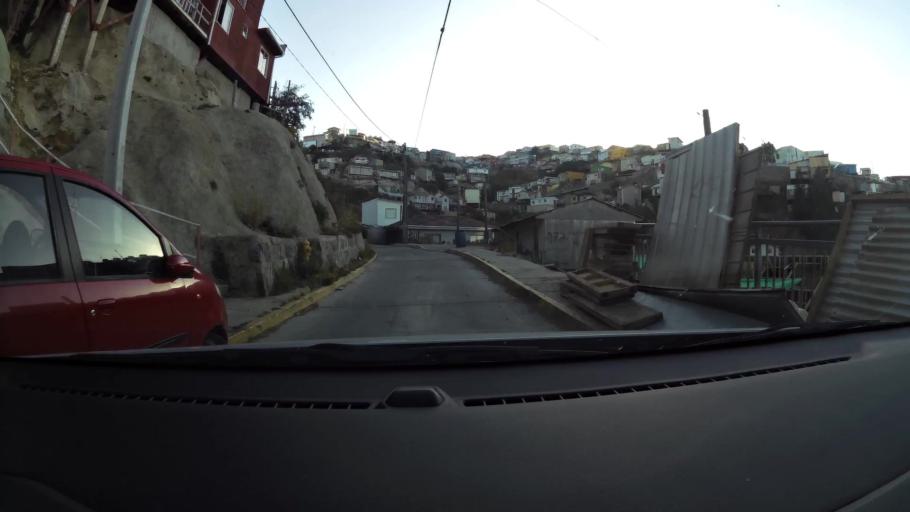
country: CL
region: Valparaiso
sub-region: Provincia de Valparaiso
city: Valparaiso
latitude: -33.0591
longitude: -71.6052
